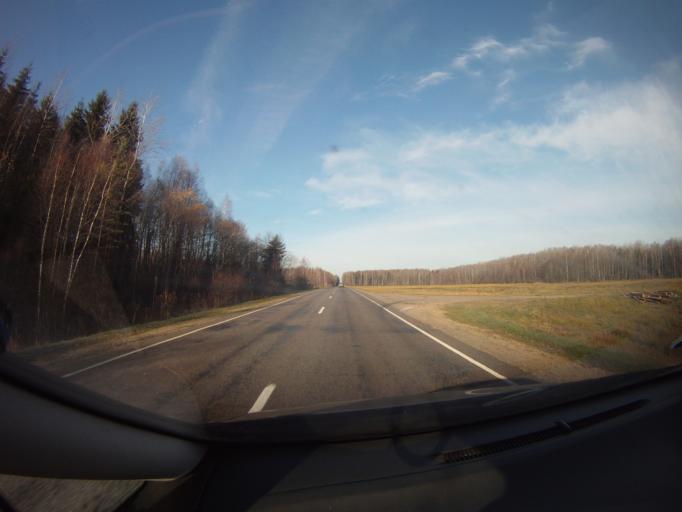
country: BY
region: Minsk
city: Il'ya
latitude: 54.3675
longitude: 27.4016
